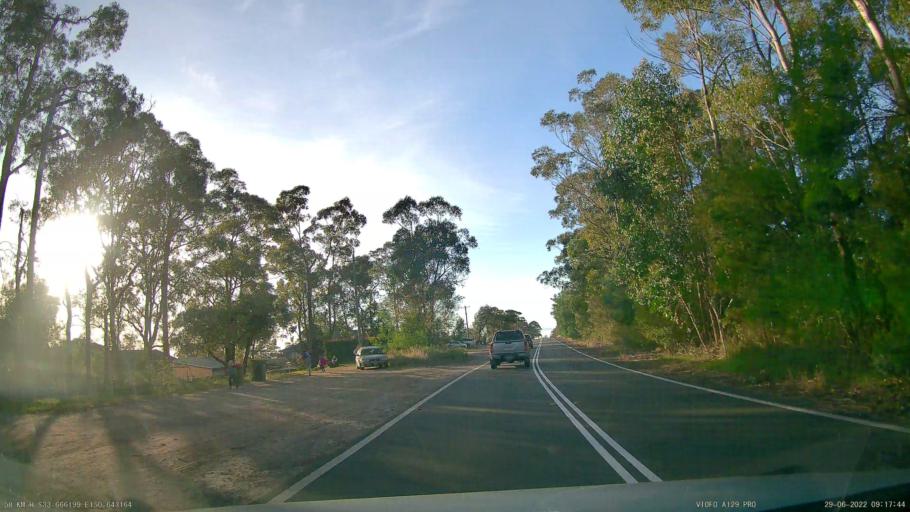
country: AU
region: New South Wales
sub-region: Penrith Municipality
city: Emu Heights
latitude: -33.6662
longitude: 150.6436
